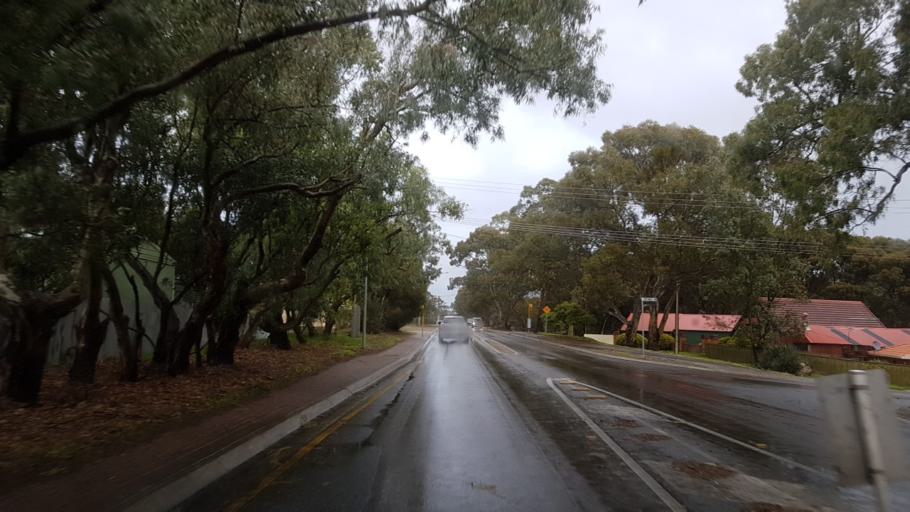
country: AU
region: South Australia
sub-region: Onkaparinga
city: Craigburn Farm
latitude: -35.0669
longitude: 138.5880
